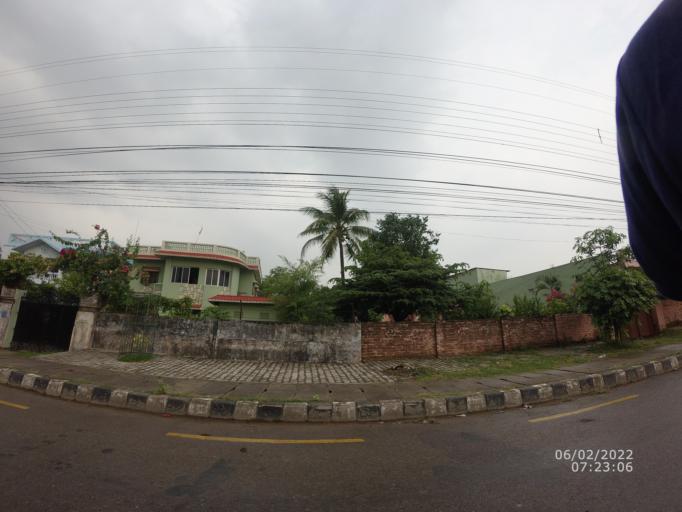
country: NP
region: Western Region
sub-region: Lumbini Zone
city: Bhairahawa
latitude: 27.4939
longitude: 83.4458
